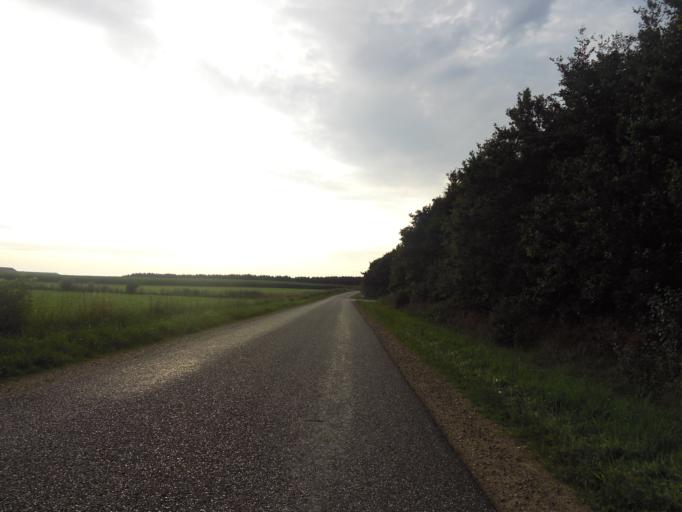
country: DK
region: South Denmark
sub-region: Tonder Kommune
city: Logumkloster
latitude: 55.1559
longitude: 8.9363
